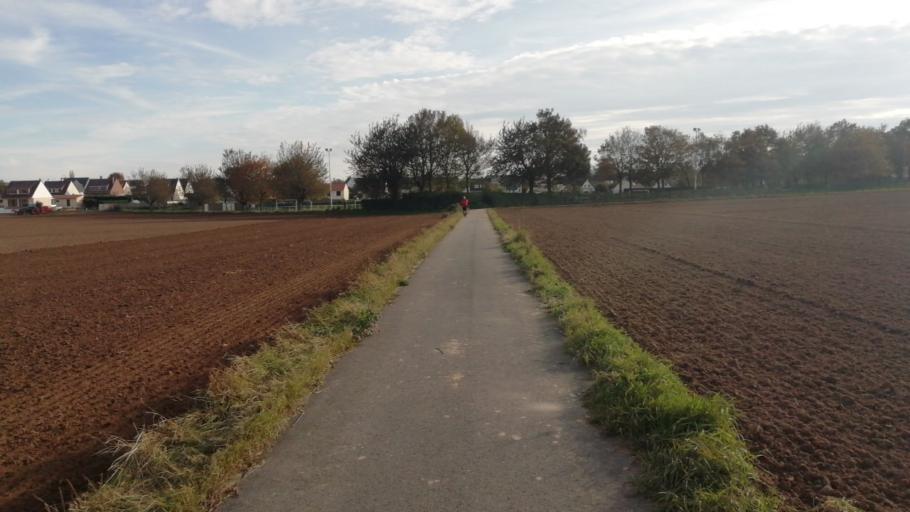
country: FR
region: Haute-Normandie
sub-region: Departement de la Seine-Maritime
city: Rogerville
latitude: 49.5086
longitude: 0.2640
